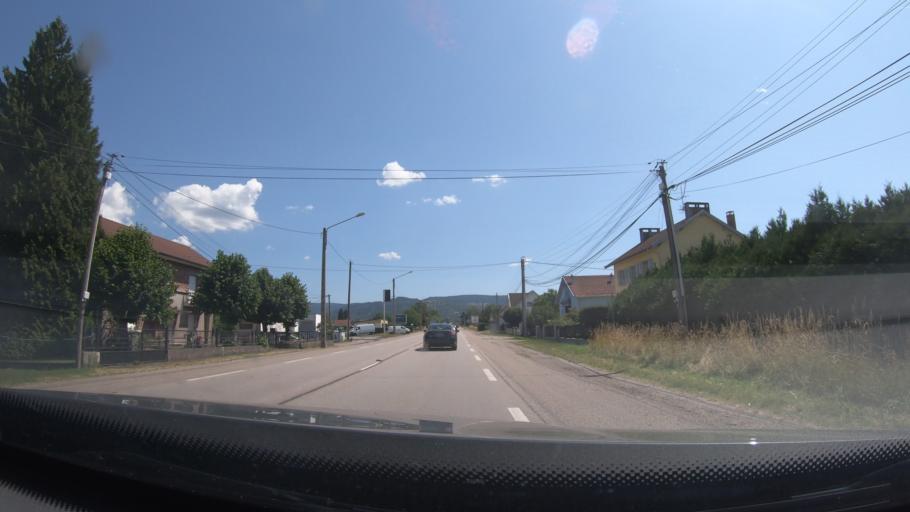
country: FR
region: Lorraine
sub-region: Departement des Vosges
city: Saint-Leonard
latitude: 48.2094
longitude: 6.9435
